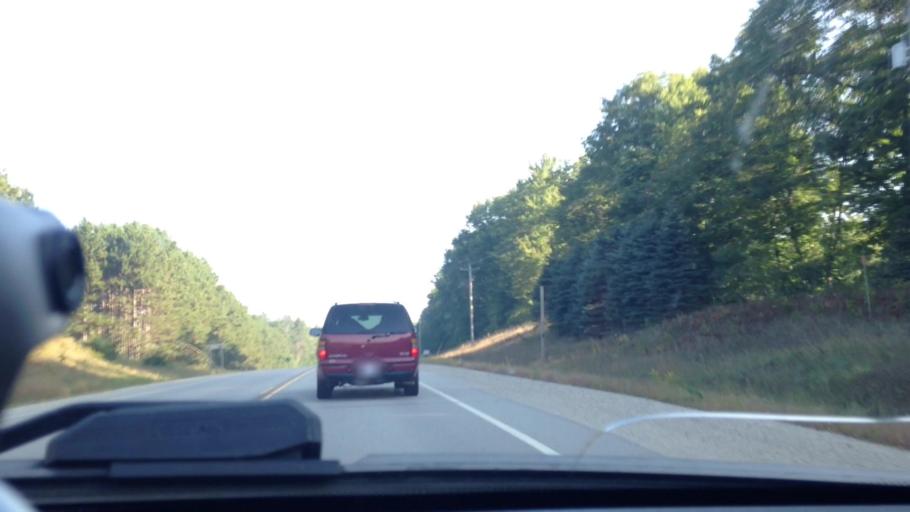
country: US
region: Wisconsin
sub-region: Marinette County
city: Peshtigo
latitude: 45.1661
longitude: -87.9964
